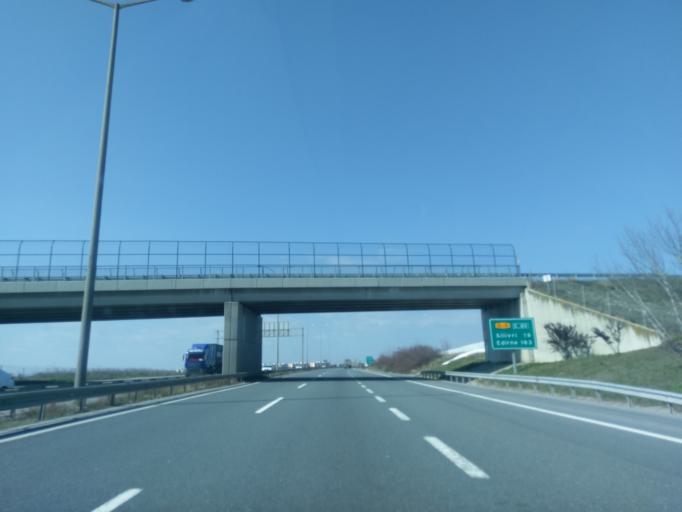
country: TR
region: Istanbul
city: Selimpasa
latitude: 41.0716
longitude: 28.3816
